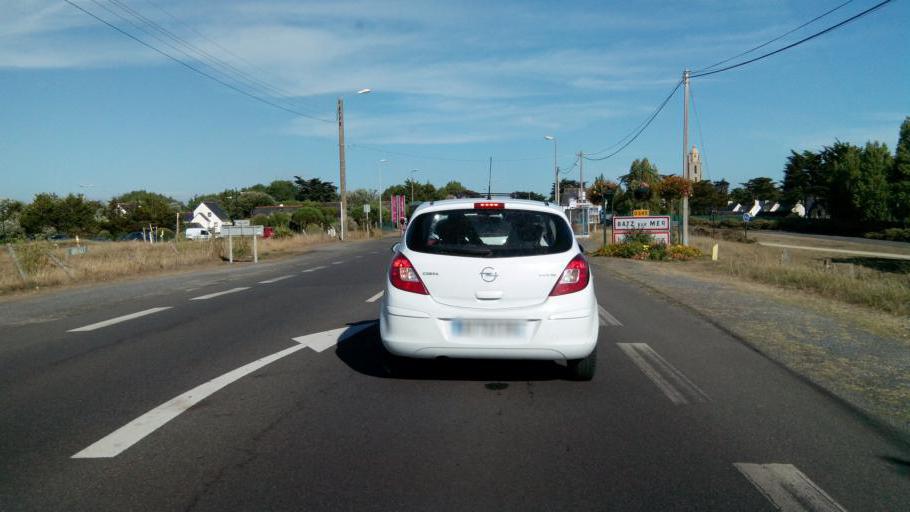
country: FR
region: Pays de la Loire
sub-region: Departement de la Loire-Atlantique
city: Batz-sur-Mer
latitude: 47.2802
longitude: -2.4893
